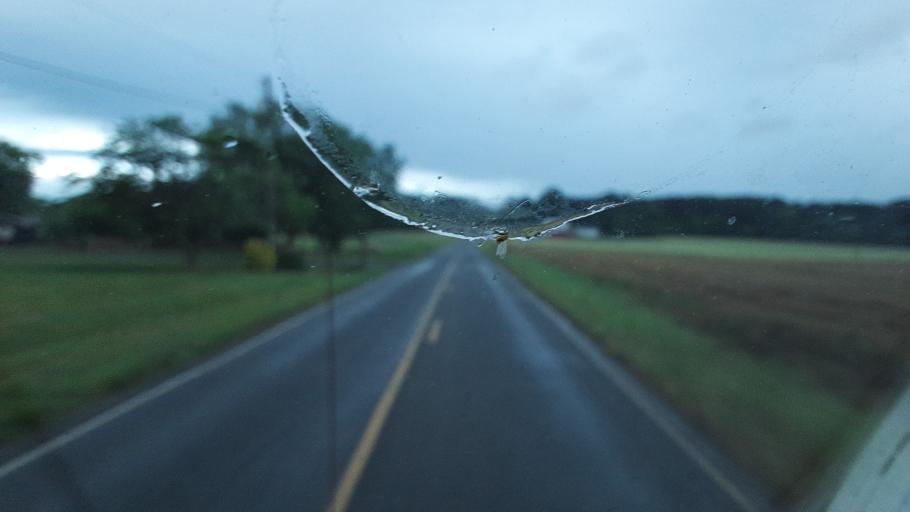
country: US
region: North Carolina
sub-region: Yadkin County
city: Jonesville
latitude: 36.1051
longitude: -80.8778
